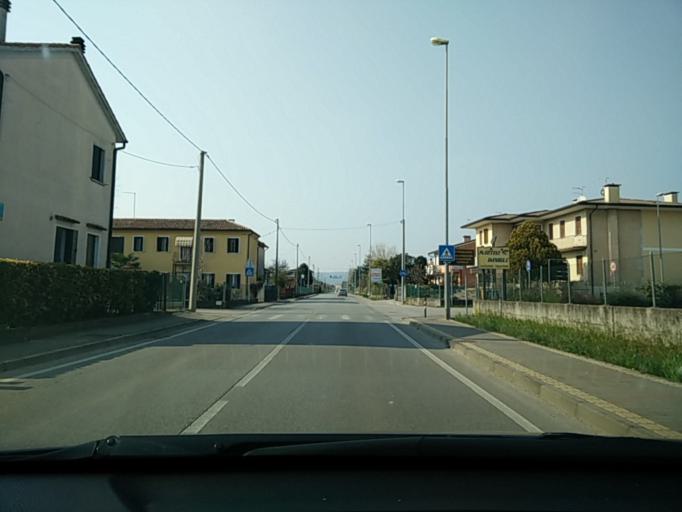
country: IT
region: Veneto
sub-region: Provincia di Treviso
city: Camalo
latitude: 45.7554
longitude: 12.1682
